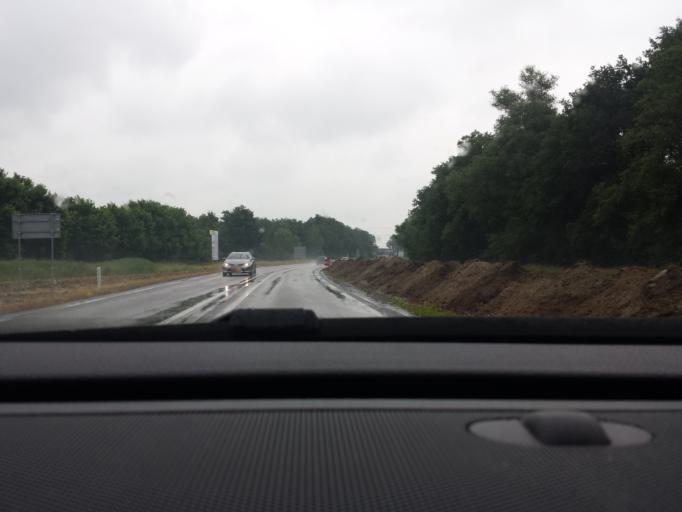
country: NL
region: Gelderland
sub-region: Berkelland
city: Borculo
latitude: 52.1172
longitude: 6.5373
